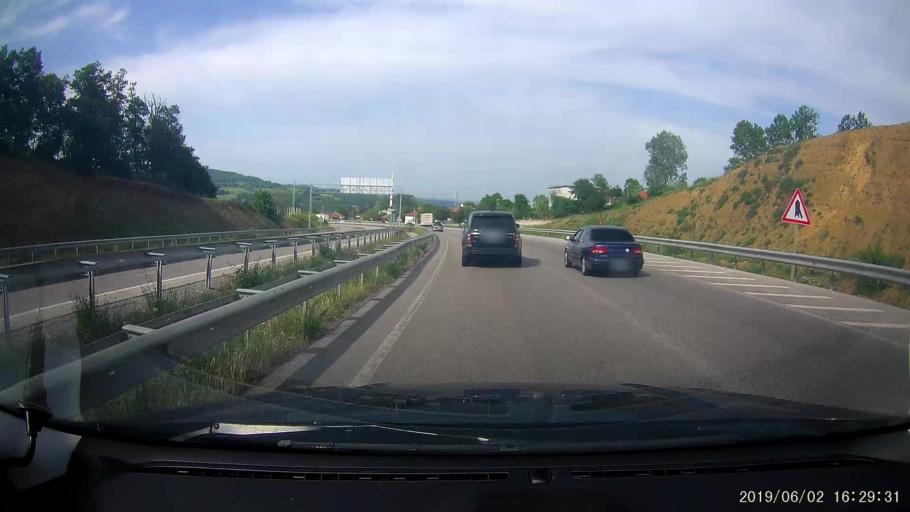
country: TR
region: Samsun
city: Ladik
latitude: 41.0139
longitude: 35.8702
